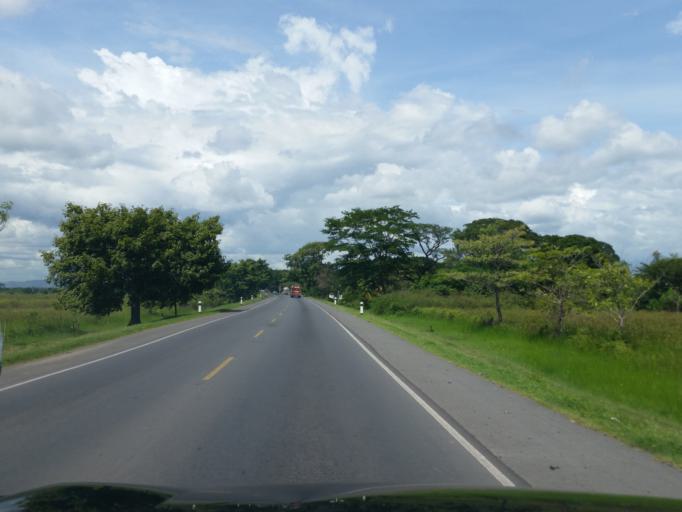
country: NI
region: Managua
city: Tipitapa
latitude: 12.1724
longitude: -86.1164
